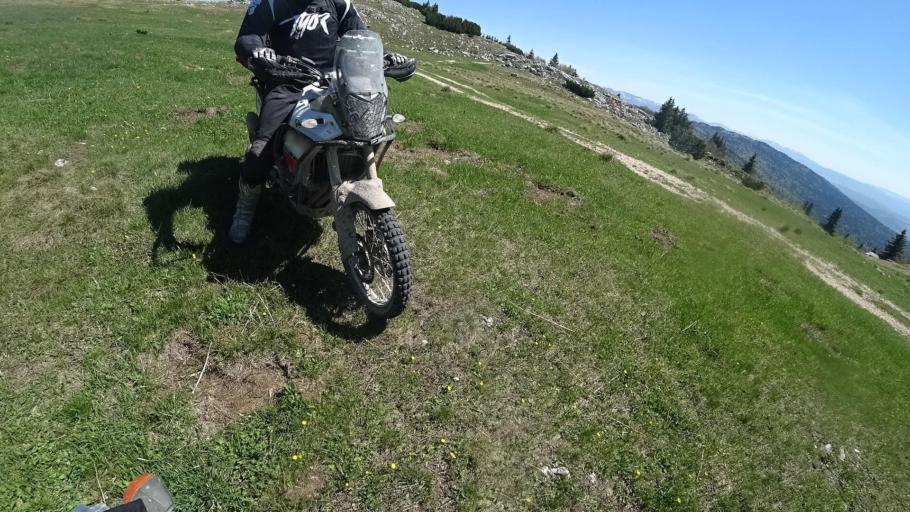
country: BA
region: Federation of Bosnia and Herzegovina
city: Rumboci
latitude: 43.8704
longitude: 17.4544
